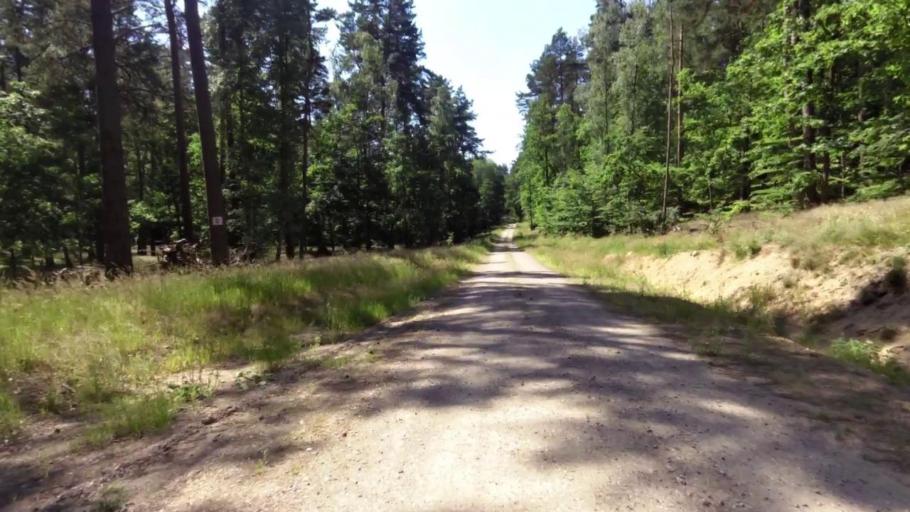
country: PL
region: West Pomeranian Voivodeship
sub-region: Powiat swidwinski
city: Polczyn-Zdroj
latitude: 53.8055
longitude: 16.1216
